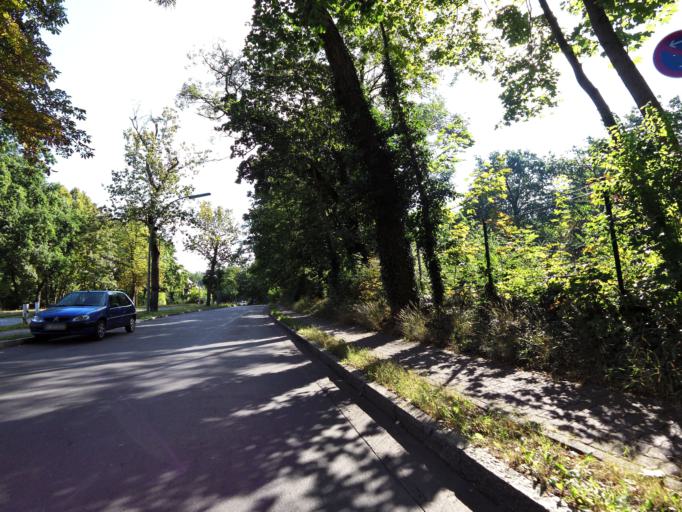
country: DE
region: Berlin
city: Nikolassee
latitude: 52.4391
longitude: 13.2098
